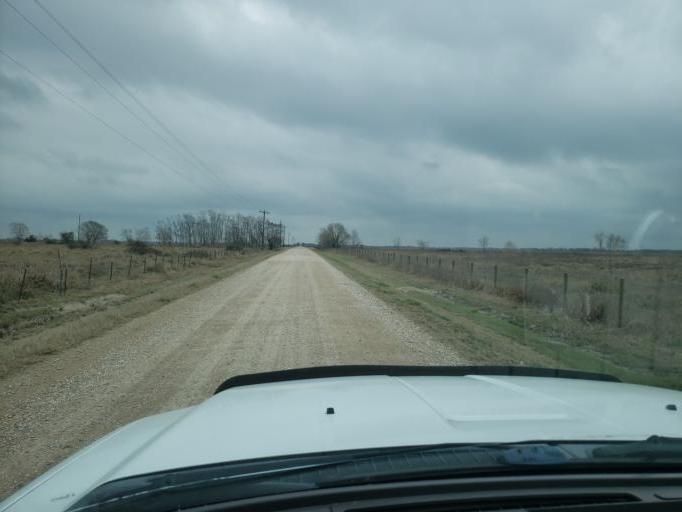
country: US
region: Texas
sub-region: Fort Bend County
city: Needville
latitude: 29.3620
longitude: -95.7360
